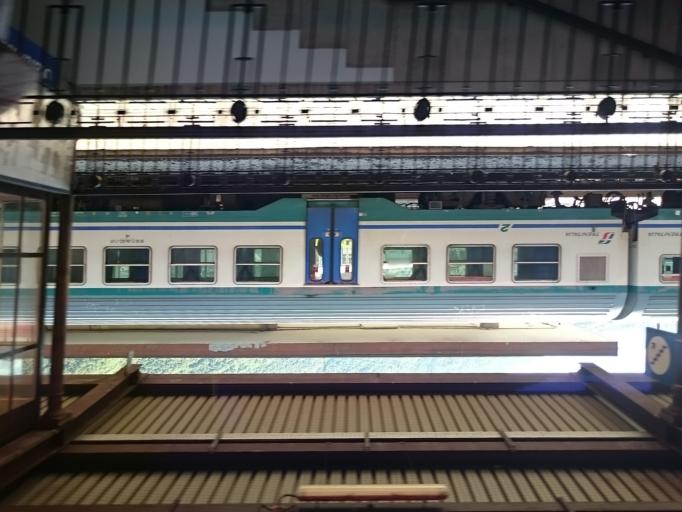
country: IT
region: Trentino-Alto Adige
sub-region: Bolzano
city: Bolzano
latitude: 46.4964
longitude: 11.3587
